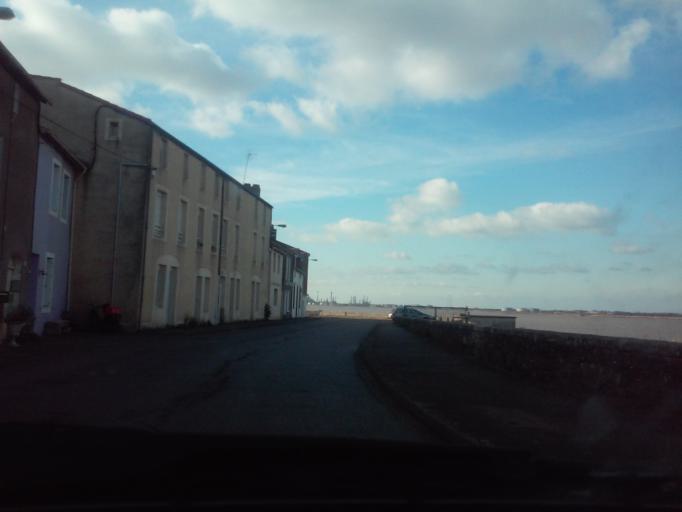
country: FR
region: Pays de la Loire
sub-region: Departement de la Loire-Atlantique
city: Saint-Paimboeuf
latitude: 47.2874
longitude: -2.0207
